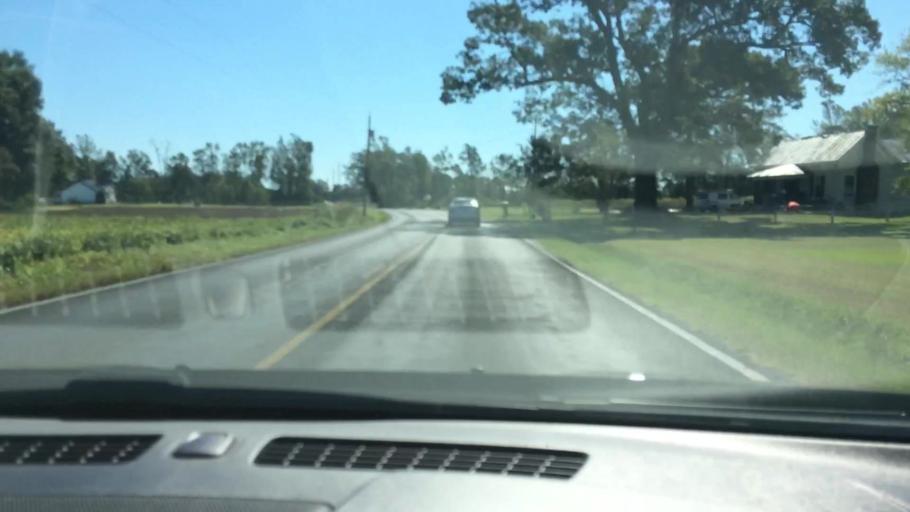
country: US
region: North Carolina
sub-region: Pitt County
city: Grifton
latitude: 35.3671
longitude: -77.3517
